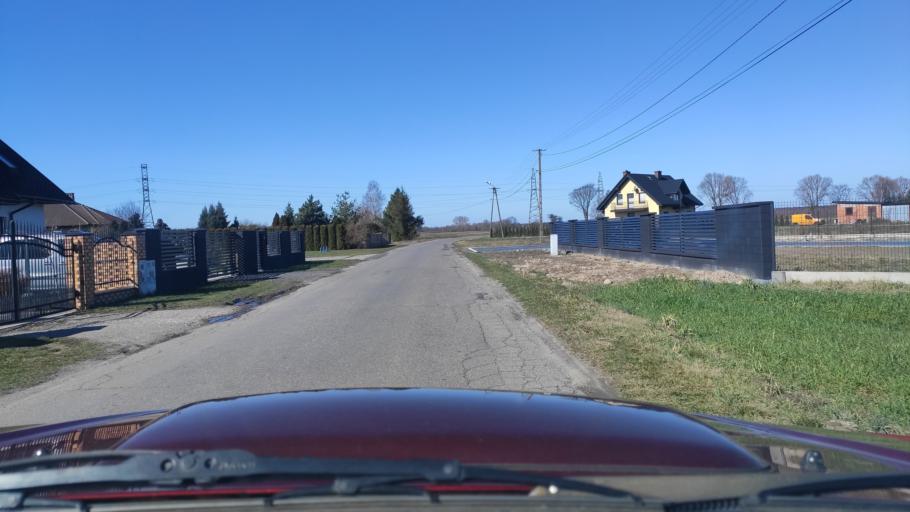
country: PL
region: Masovian Voivodeship
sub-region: Powiat zwolenski
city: Zwolen
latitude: 51.3729
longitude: 21.5845
